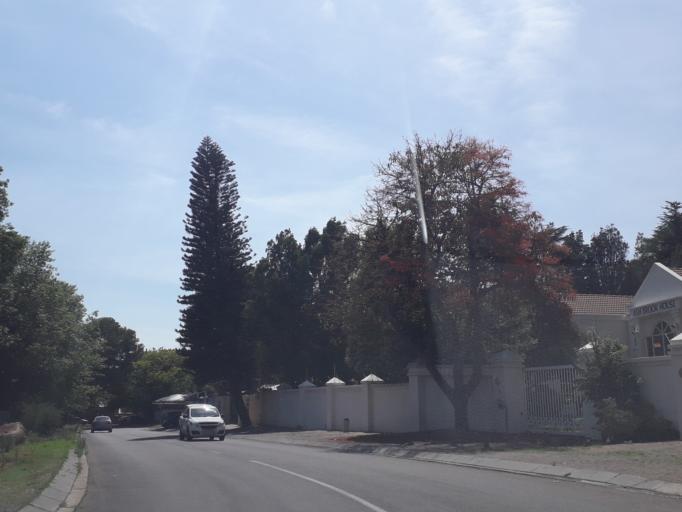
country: ZA
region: Gauteng
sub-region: City of Johannesburg Metropolitan Municipality
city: Diepsloot
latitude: -26.0405
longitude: 28.0161
